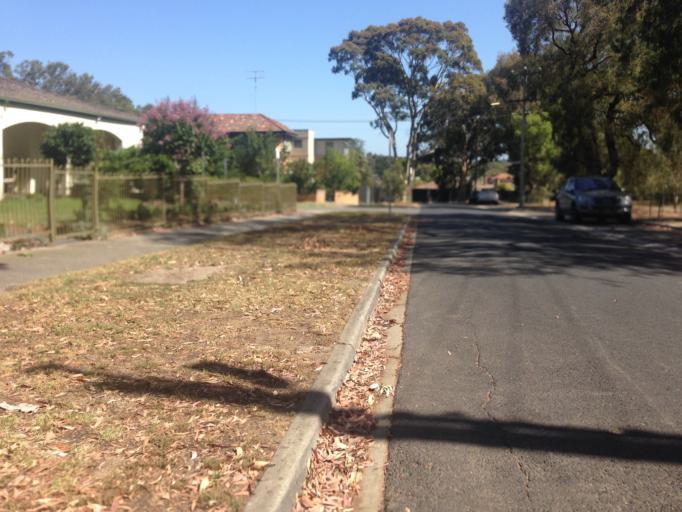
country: AU
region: Victoria
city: Ivanhoe East
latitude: -37.7730
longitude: 145.0532
